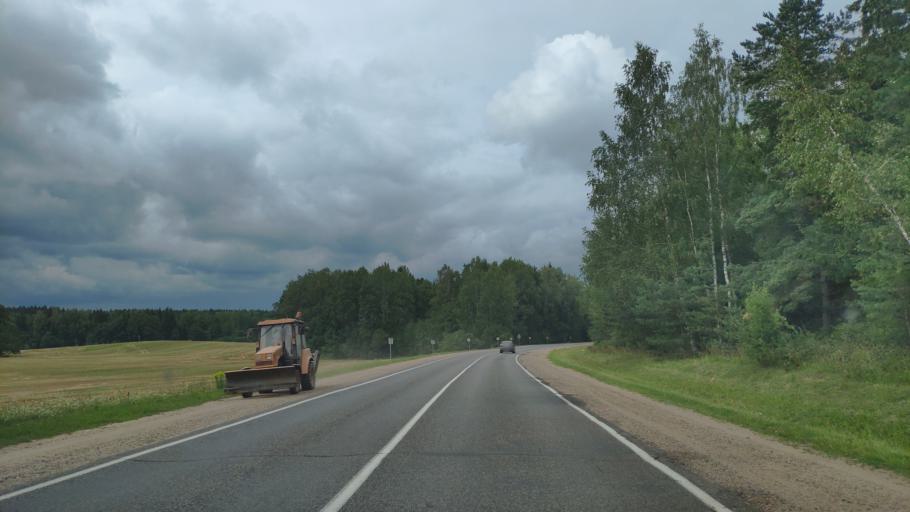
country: BY
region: Minsk
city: Zaslawye
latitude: 53.9641
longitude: 27.2446
